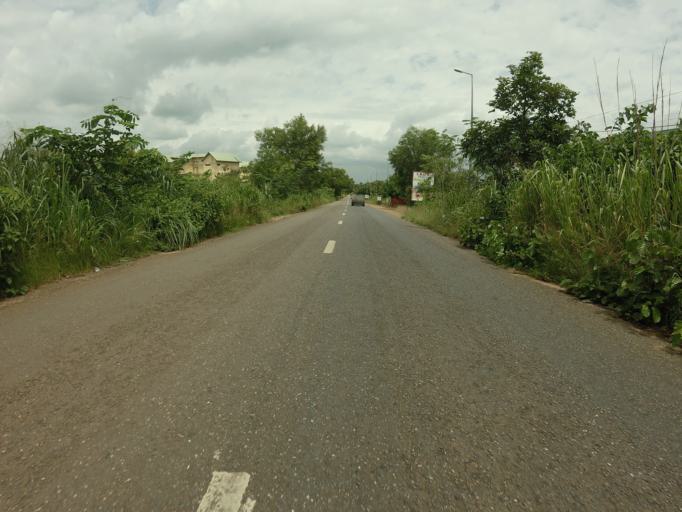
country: GH
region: Volta
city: Ho
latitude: 6.5877
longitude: 0.4629
